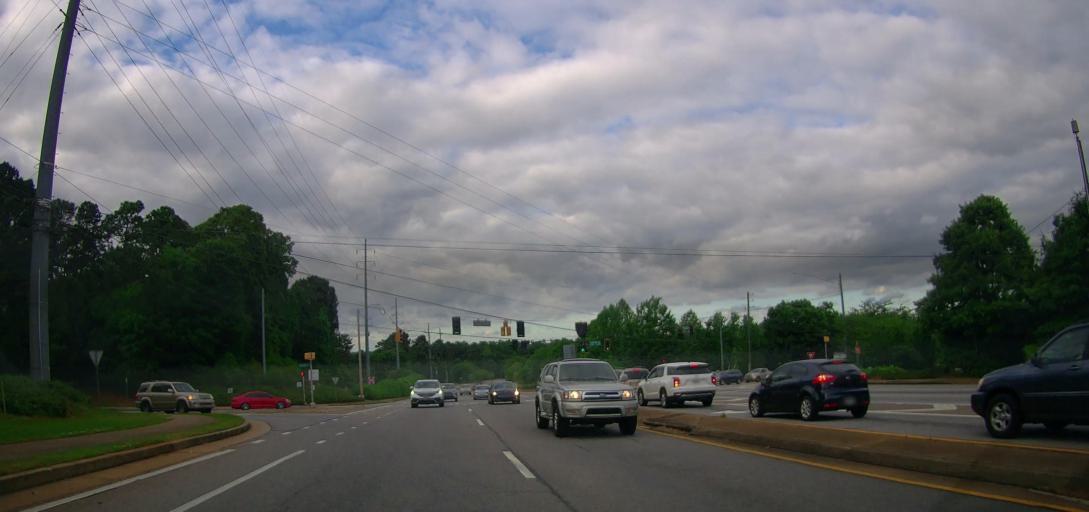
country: US
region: Georgia
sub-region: Clarke County
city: Country Club Estates
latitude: 33.9332
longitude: -83.4377
